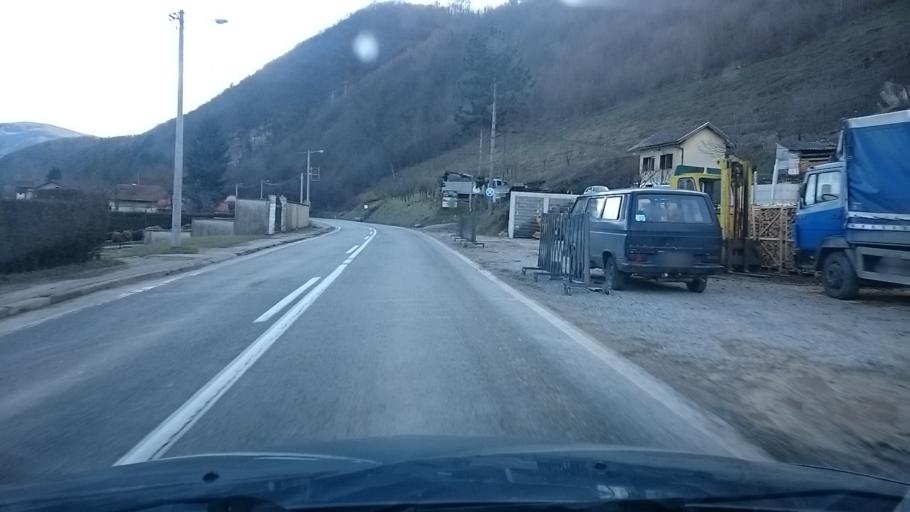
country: BA
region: Republika Srpska
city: Hiseti
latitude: 44.7311
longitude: 17.1525
